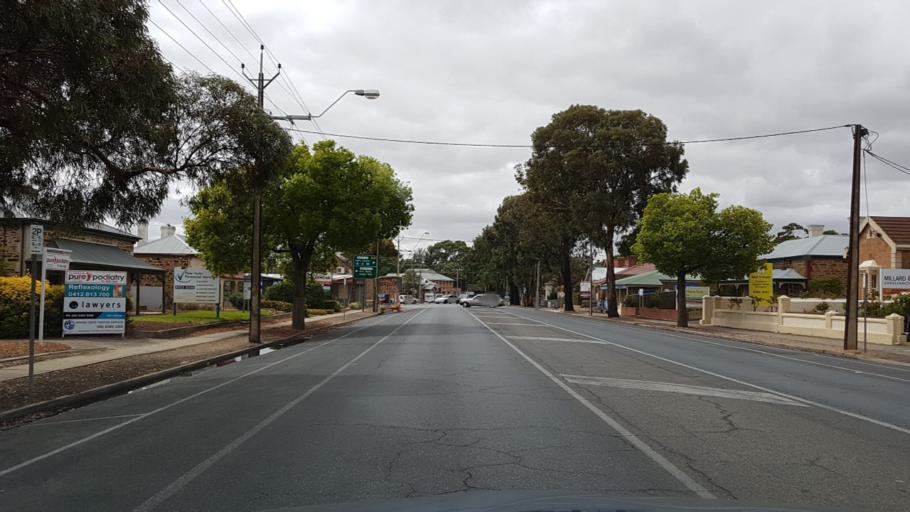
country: AU
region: South Australia
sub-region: Gawler
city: Gawler
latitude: -34.6054
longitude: 138.7451
